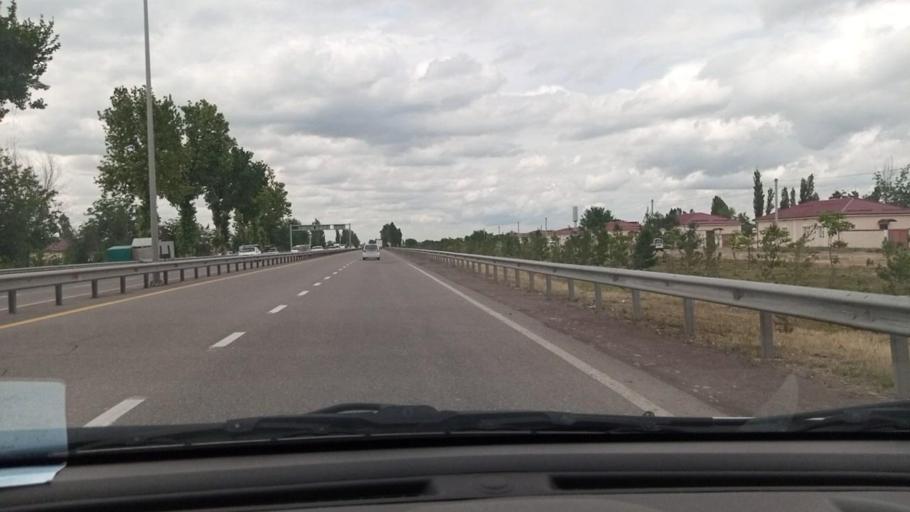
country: UZ
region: Toshkent
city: Tuytepa
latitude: 41.1333
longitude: 69.4355
